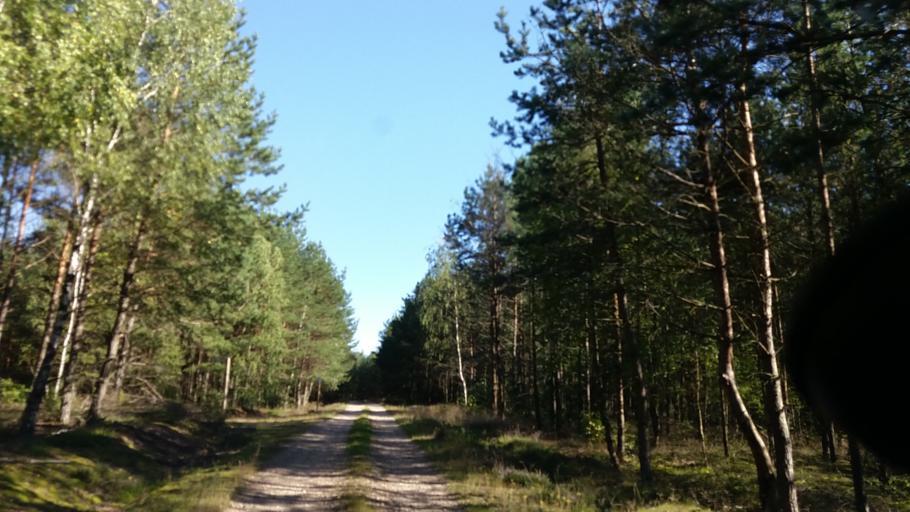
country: PL
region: West Pomeranian Voivodeship
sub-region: Powiat szczecinecki
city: Borne Sulinowo
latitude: 53.5709
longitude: 16.4906
